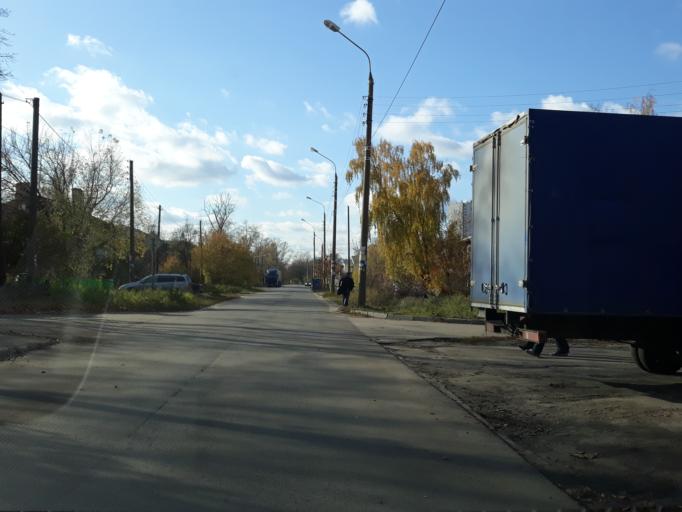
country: RU
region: Nizjnij Novgorod
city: Nizhniy Novgorod
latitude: 56.3029
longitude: 43.9350
